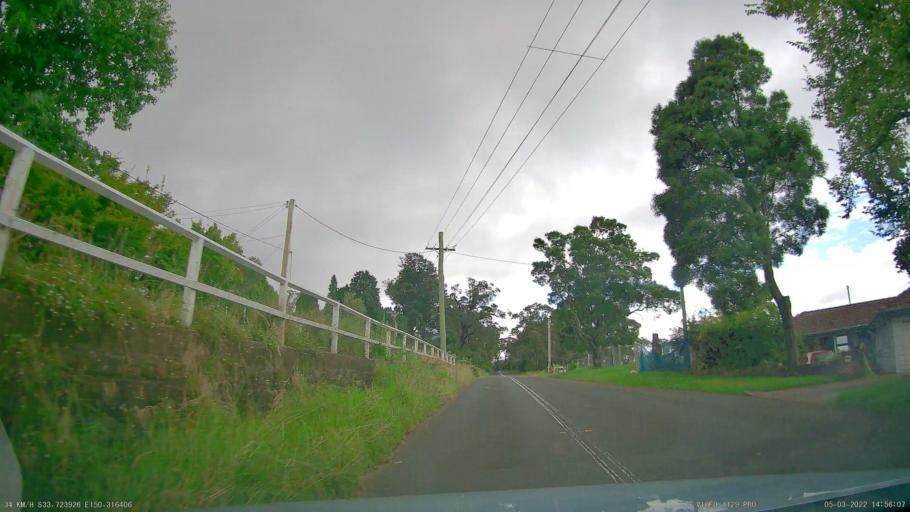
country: AU
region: New South Wales
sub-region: Blue Mountains Municipality
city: Katoomba
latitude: -33.7237
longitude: 150.3165
